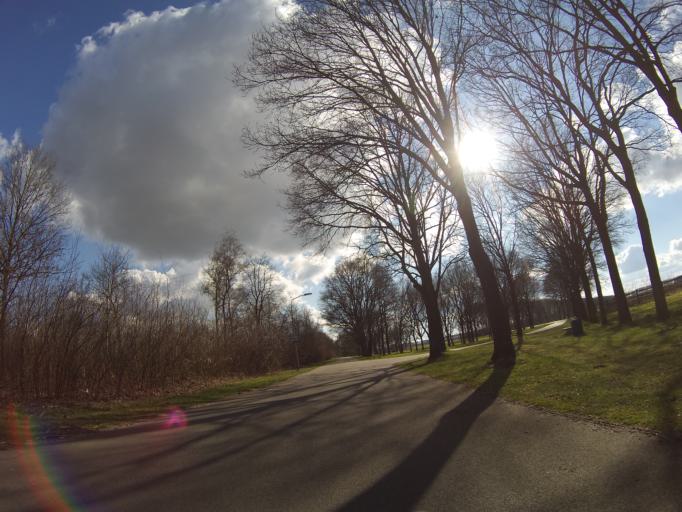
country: NL
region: Drenthe
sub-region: Gemeente Coevorden
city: Sleen
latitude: 52.7706
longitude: 6.7948
